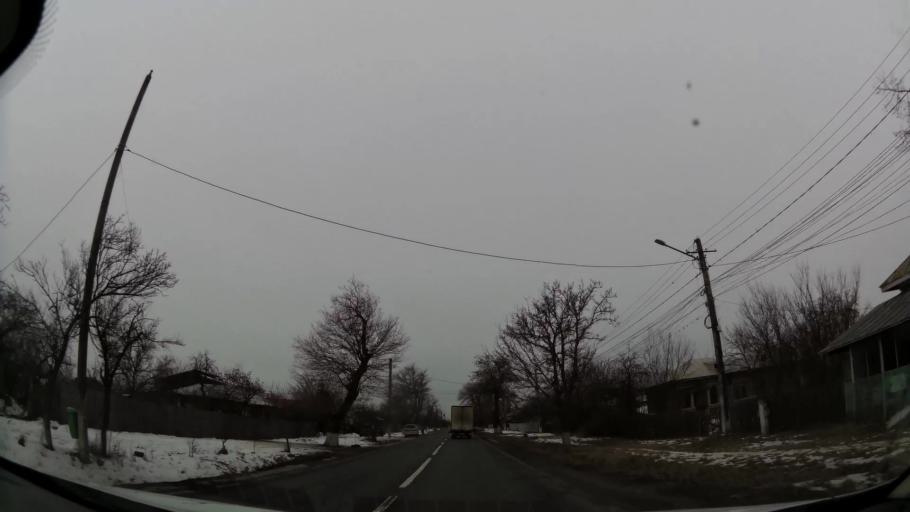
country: RO
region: Dambovita
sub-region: Comuna Tartasesti
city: Baldana
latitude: 44.5993
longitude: 25.7829
